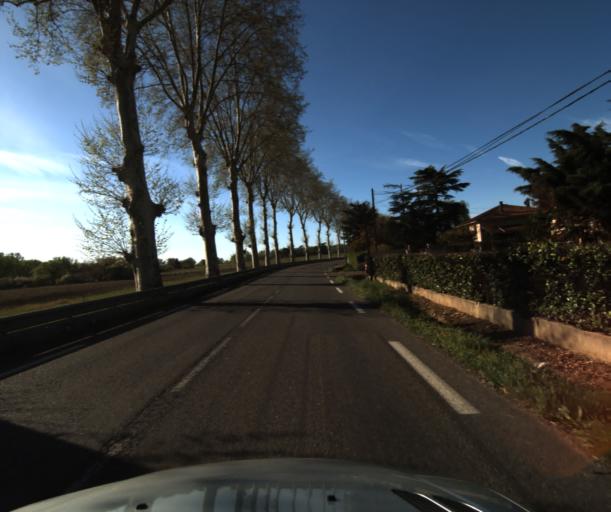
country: FR
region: Midi-Pyrenees
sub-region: Departement du Tarn-et-Garonne
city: Lafrancaise
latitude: 44.0835
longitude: 1.2757
